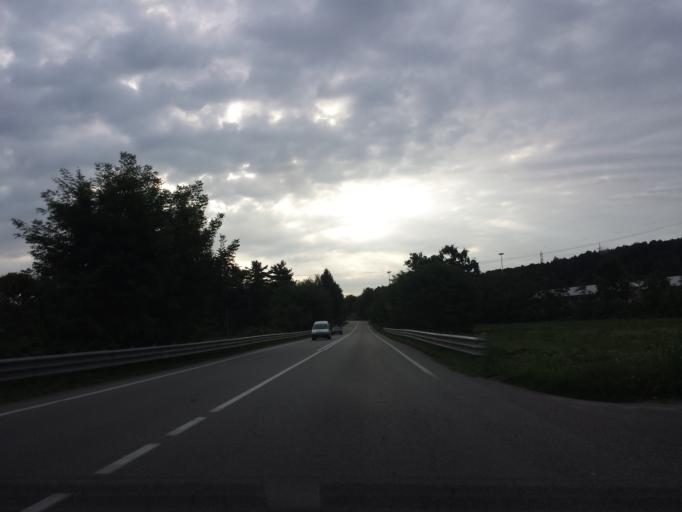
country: IT
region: Lombardy
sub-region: Provincia di Varese
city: Golasecca
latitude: 45.7221
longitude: 8.6650
